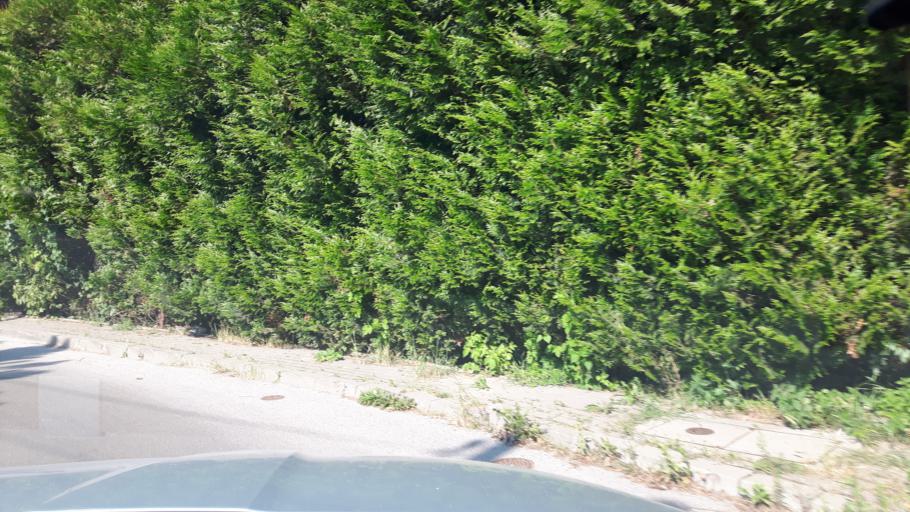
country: PL
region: Masovian Voivodeship
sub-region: Warszawa
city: Wlochy
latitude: 52.2100
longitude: 20.9335
